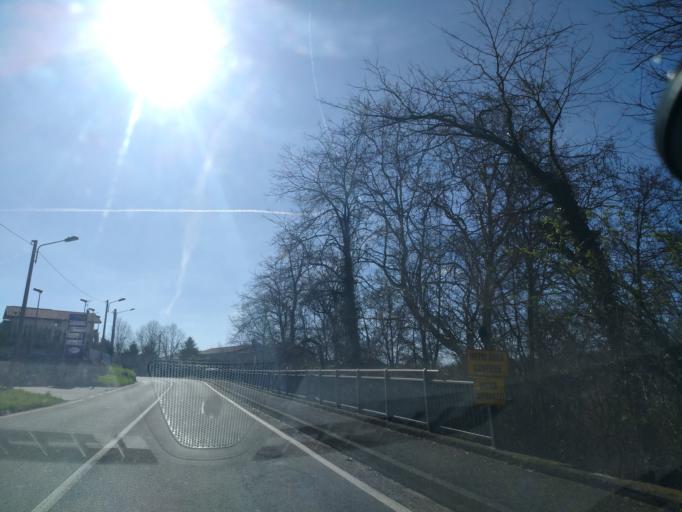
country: IT
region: Lombardy
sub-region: Provincia di Como
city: Lipomo
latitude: 45.7899
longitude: 9.1282
